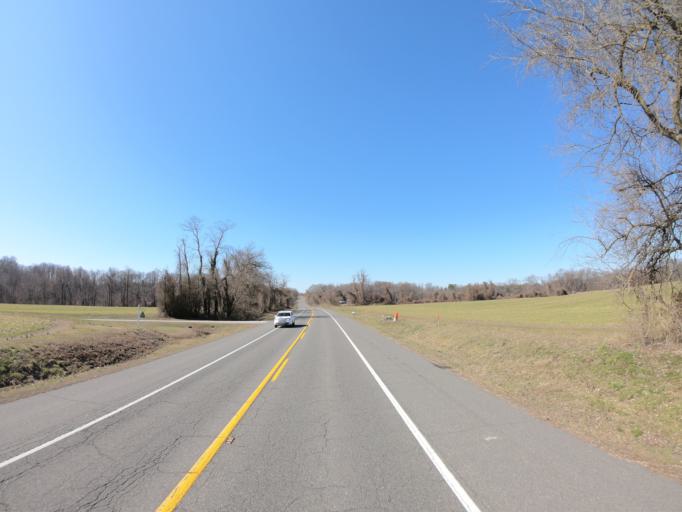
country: US
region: Delaware
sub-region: New Castle County
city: Townsend
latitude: 39.3435
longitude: -75.8622
